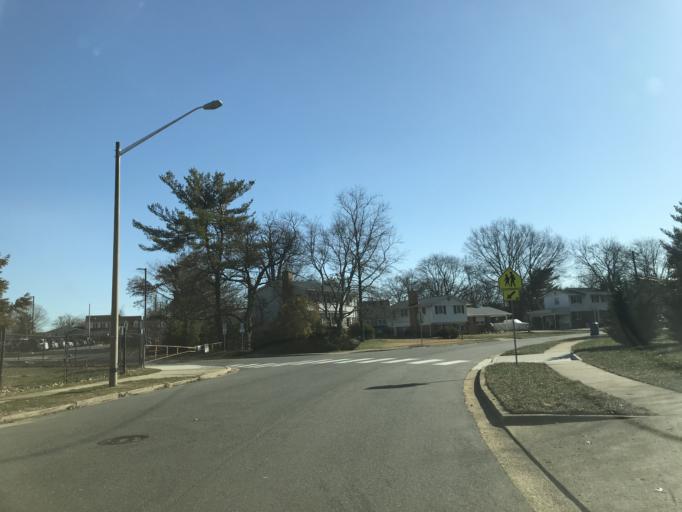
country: US
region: Virginia
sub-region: Fairfax County
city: Franconia
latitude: 38.7834
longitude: -77.1651
